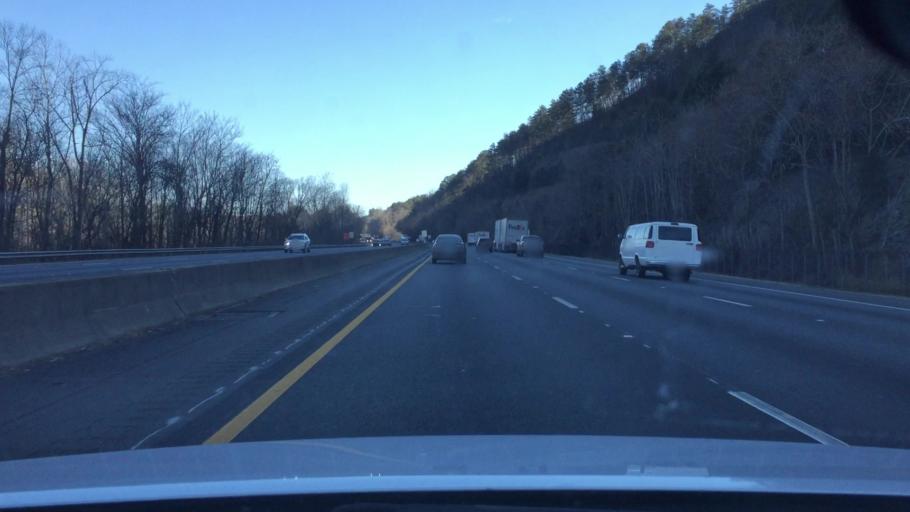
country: US
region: Georgia
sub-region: Catoosa County
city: Ringgold
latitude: 34.9074
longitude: -85.1037
